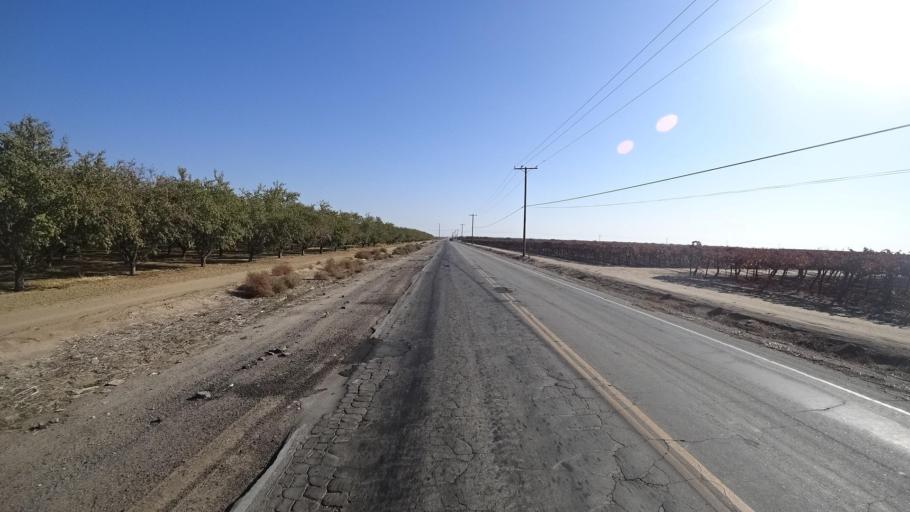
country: US
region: California
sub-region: Kern County
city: McFarland
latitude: 35.7180
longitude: -119.2274
